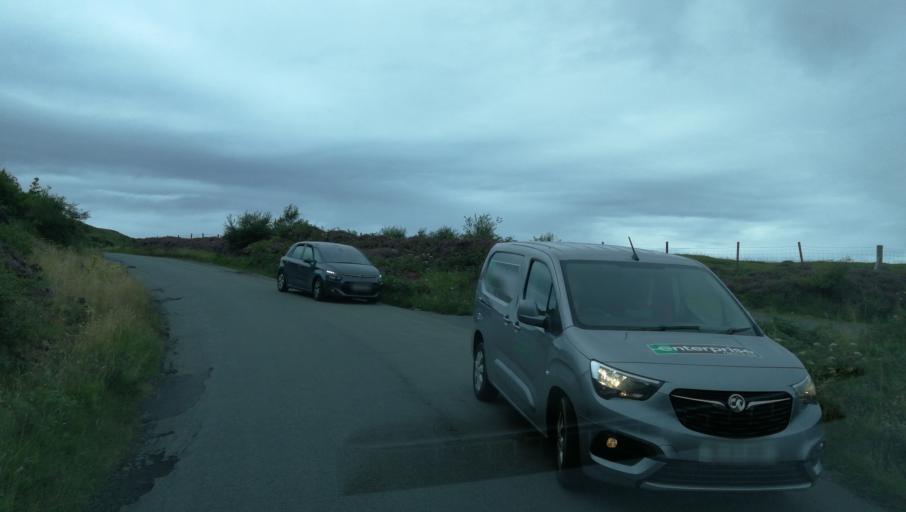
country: GB
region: Scotland
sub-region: Highland
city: Portree
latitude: 57.6466
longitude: -6.2431
